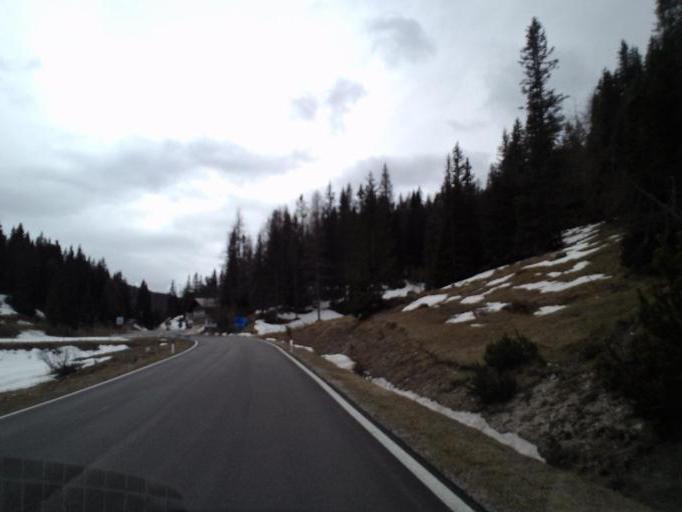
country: IT
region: Veneto
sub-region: Provincia di Belluno
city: Cortina d'Ampezzo
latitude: 46.5885
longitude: 12.2531
